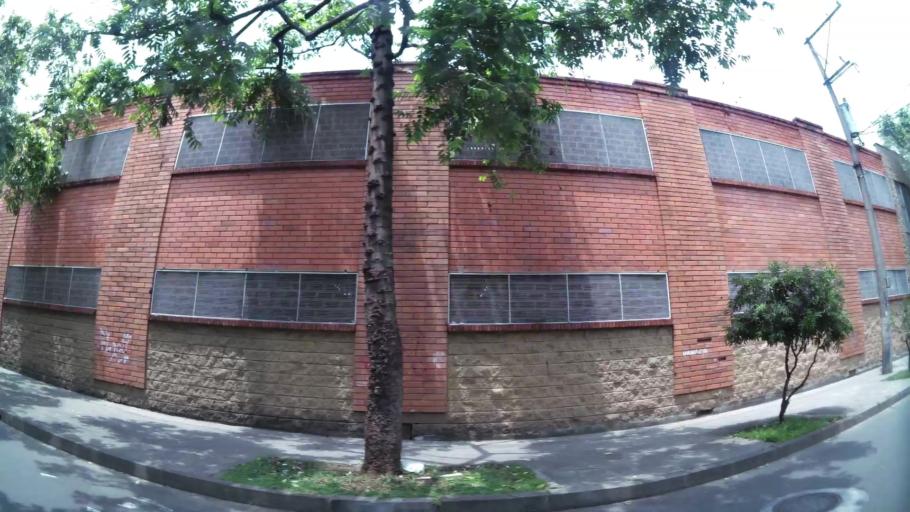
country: CO
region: Antioquia
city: Sabaneta
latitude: 6.1688
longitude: -75.6103
